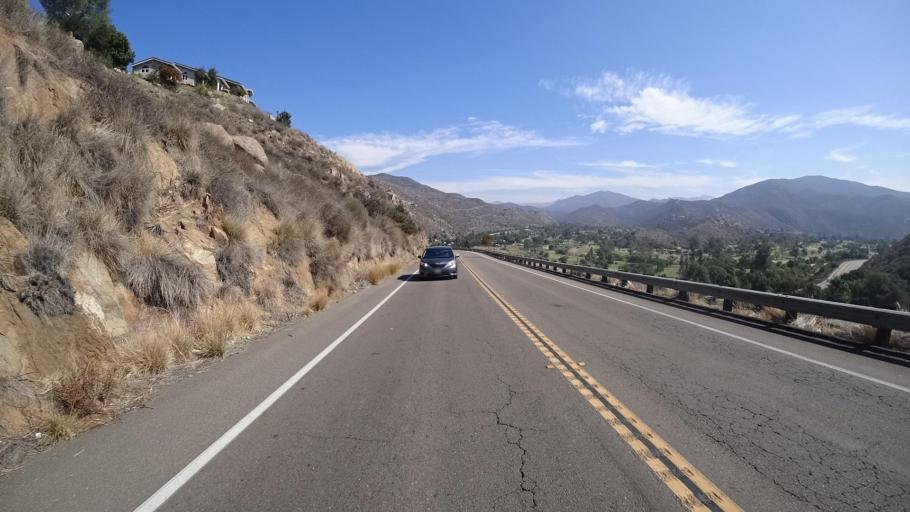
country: US
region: California
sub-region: San Diego County
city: Granite Hills
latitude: 32.7852
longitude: -116.8918
